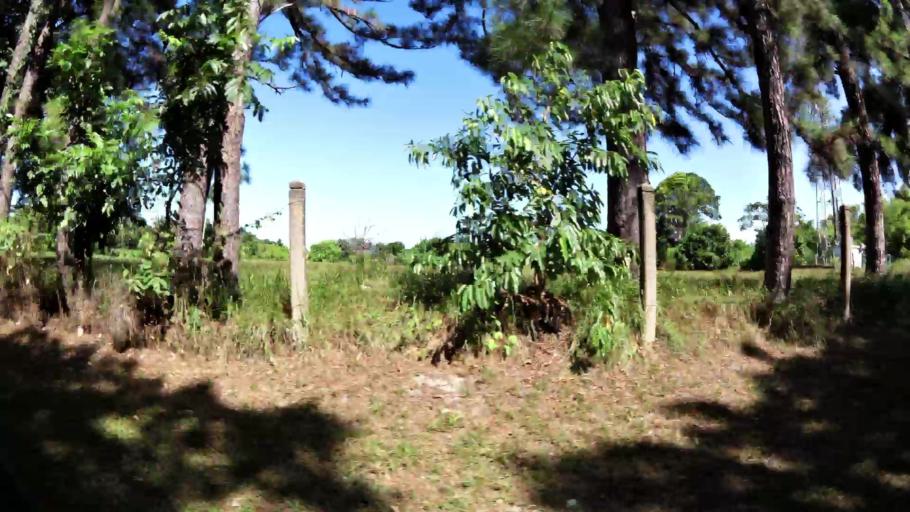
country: GF
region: Guyane
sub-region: Guyane
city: Remire-Montjoly
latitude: 4.9141
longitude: -52.2672
